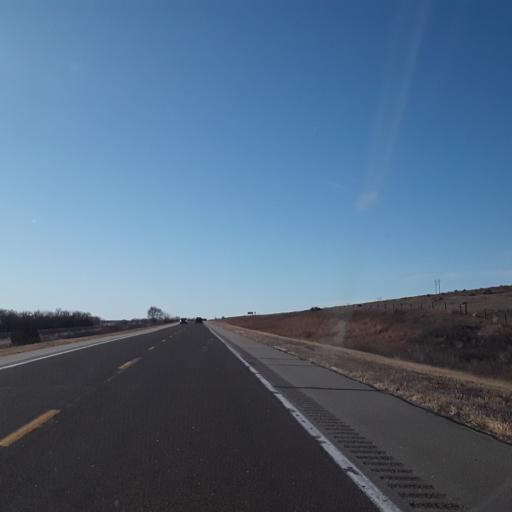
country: US
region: Nebraska
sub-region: Hitchcock County
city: Trenton
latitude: 40.1573
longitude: -101.1775
